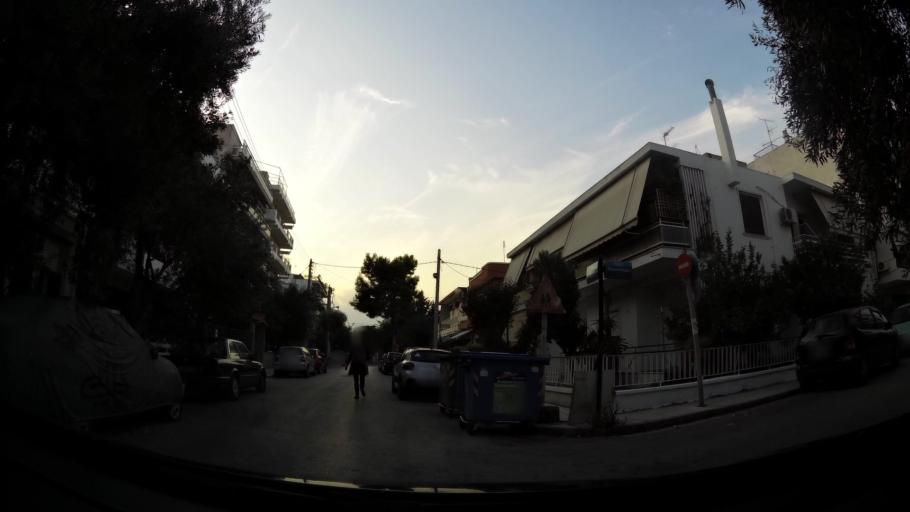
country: GR
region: Attica
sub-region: Nomarchia Athinas
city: Moskhaton
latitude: 37.9496
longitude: 23.6810
